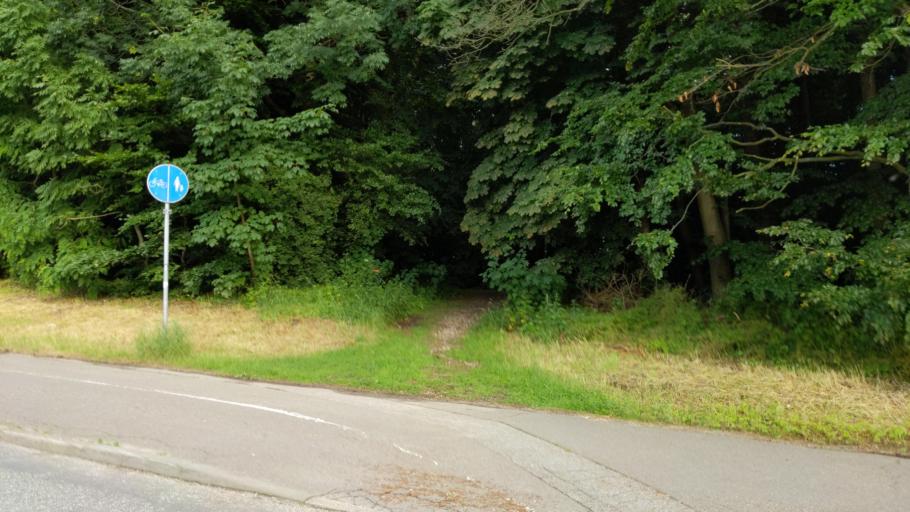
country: DE
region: Mecklenburg-Vorpommern
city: Selmsdorf
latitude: 53.9118
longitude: 10.7984
